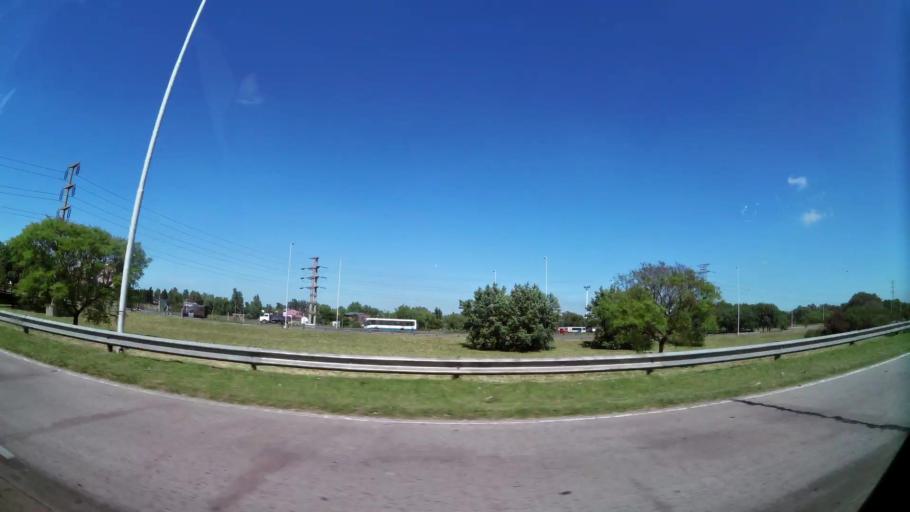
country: AR
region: Buenos Aires
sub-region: Partido de Tigre
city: Tigre
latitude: -34.4375
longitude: -58.5848
